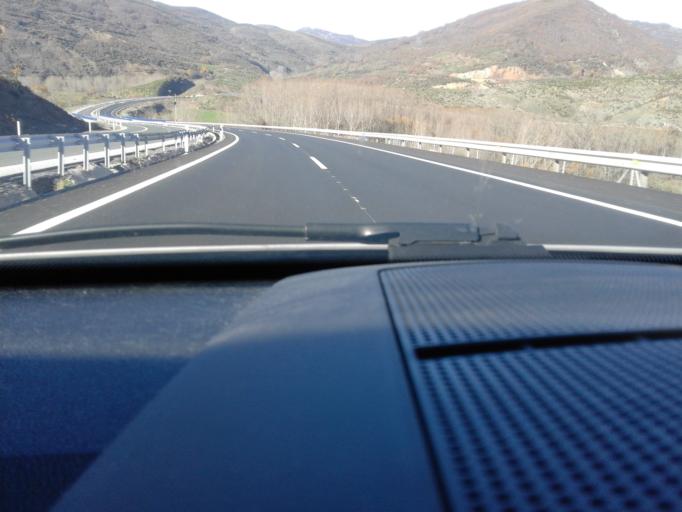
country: ES
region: Castille and Leon
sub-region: Provincia de Leon
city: Soto y Amio
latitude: 42.8236
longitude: -5.8642
